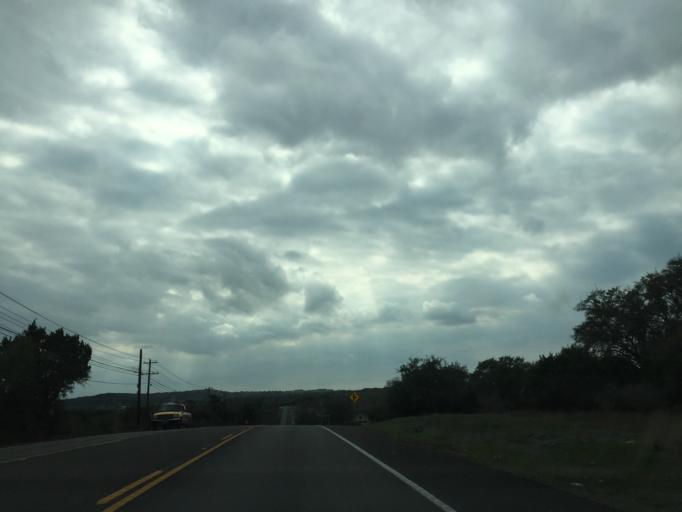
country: US
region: Texas
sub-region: Travis County
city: Shady Hollow
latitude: 30.1659
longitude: -97.9462
